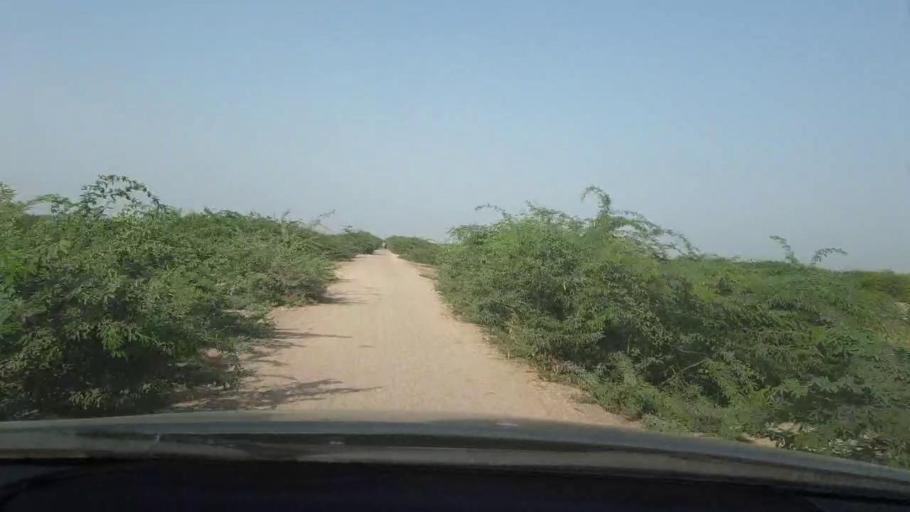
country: PK
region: Sindh
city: Naukot
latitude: 24.7913
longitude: 69.2986
